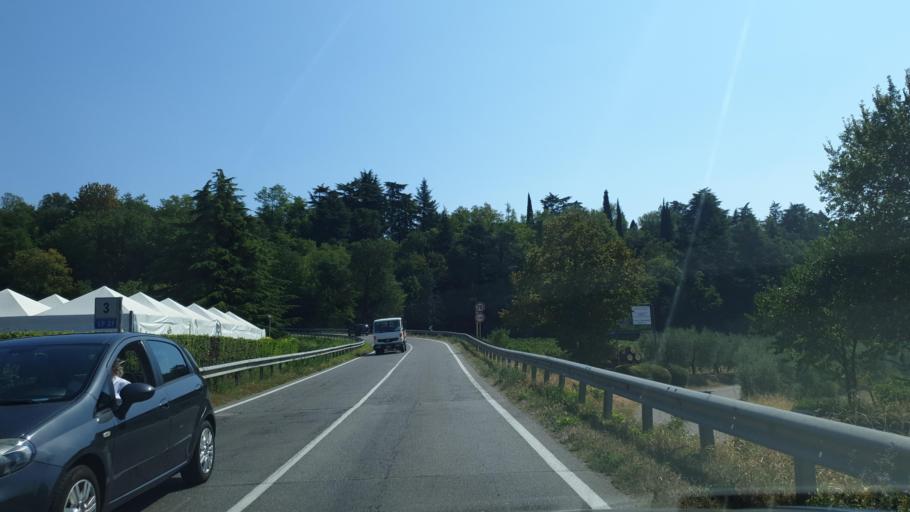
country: IT
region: Lombardy
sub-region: Provincia di Brescia
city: Calvagese della Riviera
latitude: 45.5426
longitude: 10.4405
